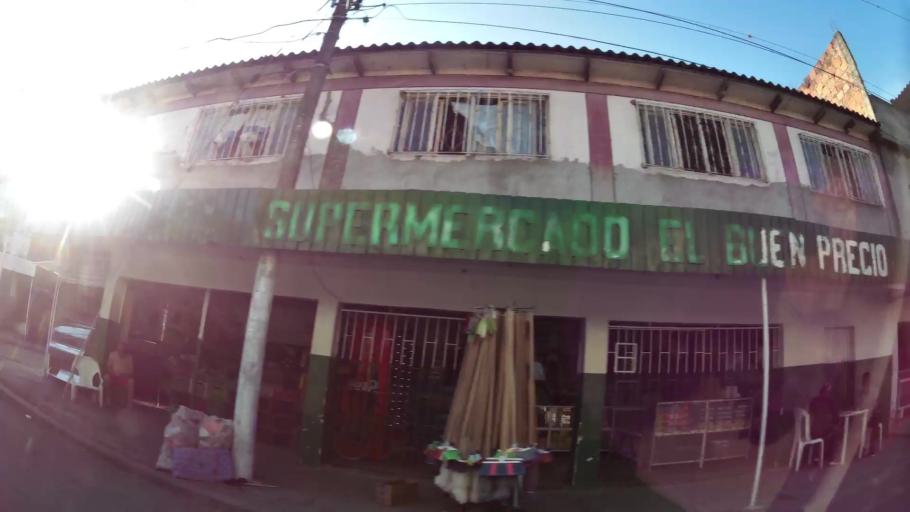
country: CO
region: Valle del Cauca
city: Cali
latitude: 3.4091
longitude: -76.5005
